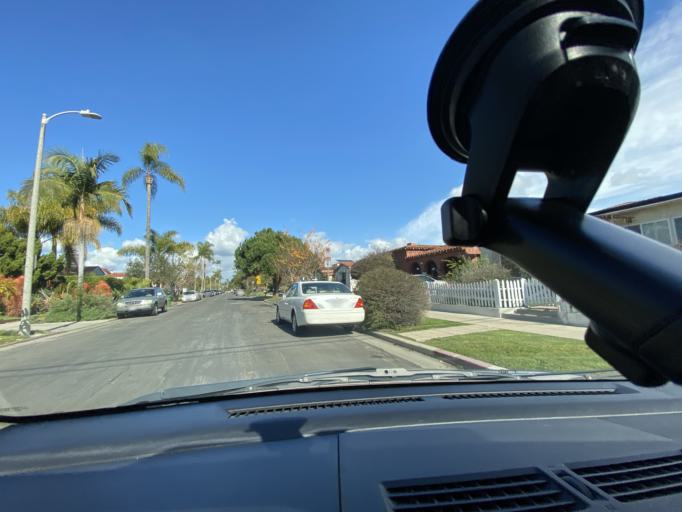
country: US
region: California
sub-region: Los Angeles County
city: Culver City
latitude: 34.0448
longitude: -118.3780
